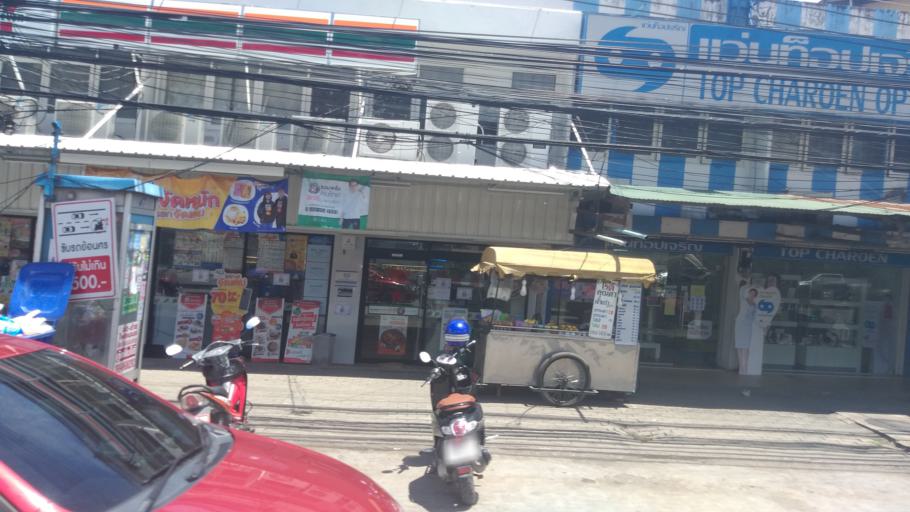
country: TH
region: Nakhon Nayok
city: Ban Na
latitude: 14.2608
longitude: 101.0706
